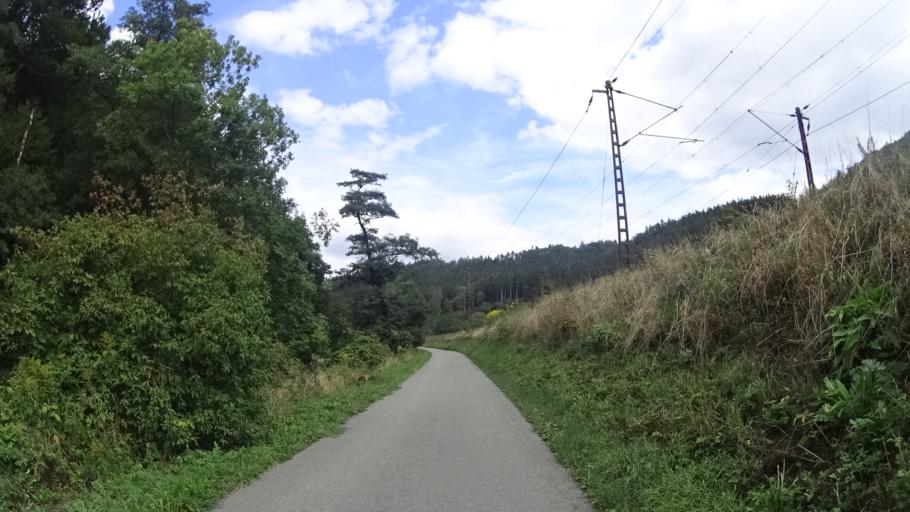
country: CZ
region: Pardubicky
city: Brandys nad Orlici
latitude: 49.9805
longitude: 16.3355
